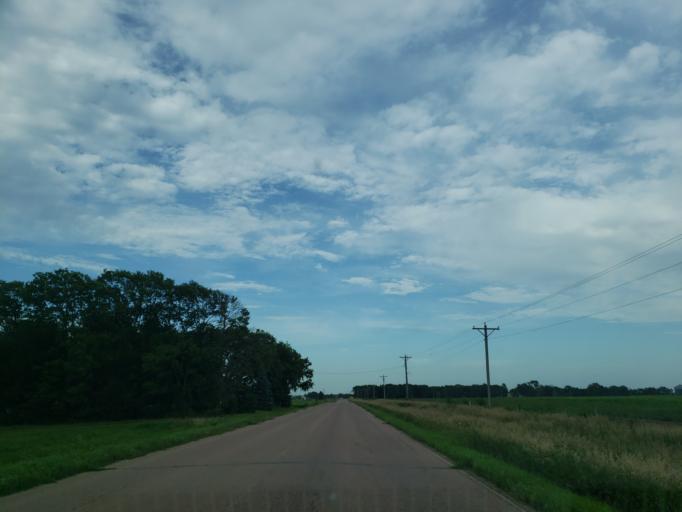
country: US
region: South Dakota
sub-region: Davison County
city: Mitchell
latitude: 43.6878
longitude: -97.9941
